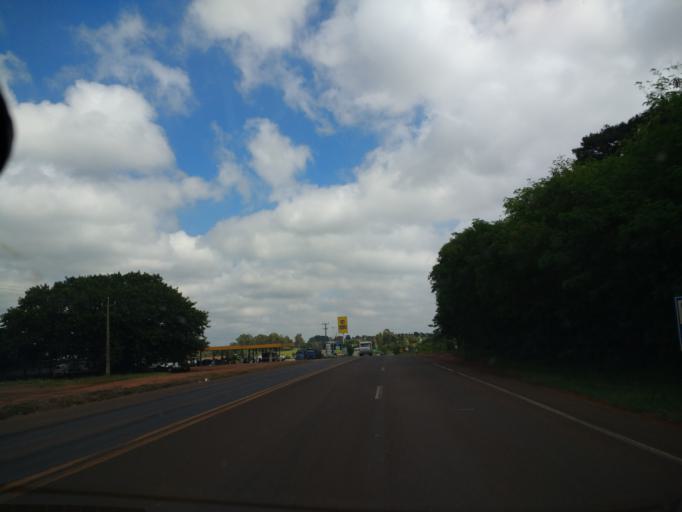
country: BR
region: Parana
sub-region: Cruzeiro Do Oeste
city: Cruzeiro do Oeste
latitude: -23.7920
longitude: -53.0406
